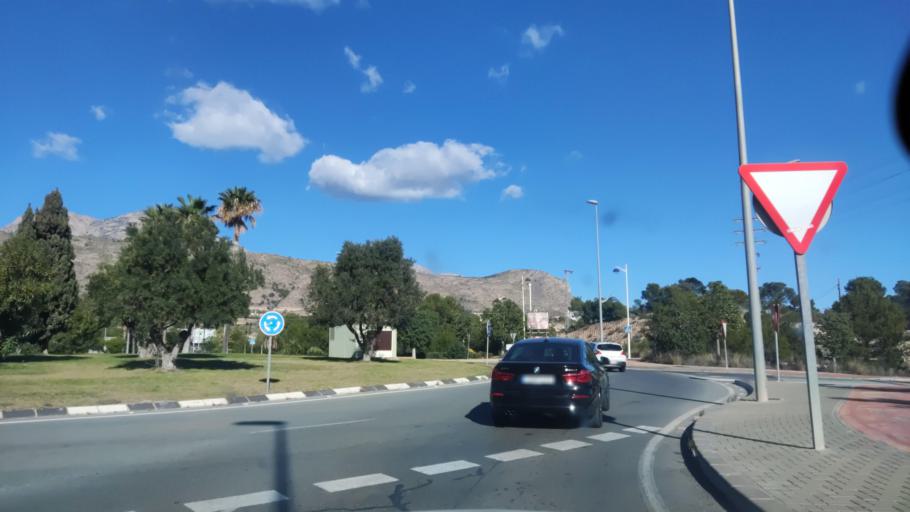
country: ES
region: Valencia
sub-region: Provincia de Alicante
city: Benidorm
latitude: 38.5451
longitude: -0.1609
